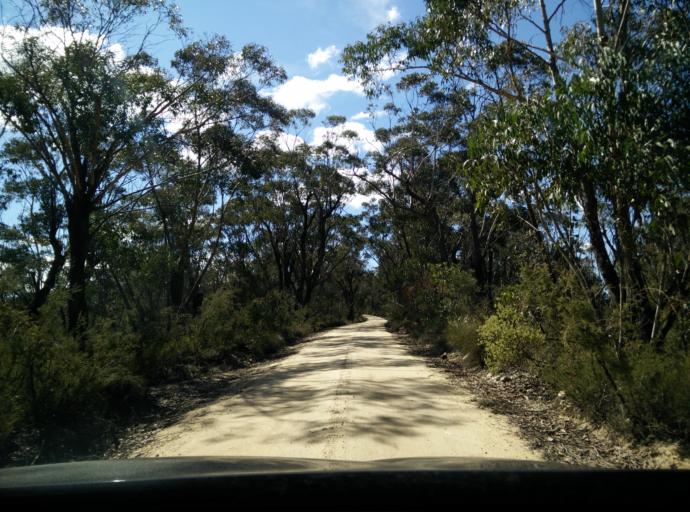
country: AU
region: New South Wales
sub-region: Blue Mountains Municipality
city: Blackheath
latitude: -33.5714
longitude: 150.2882
